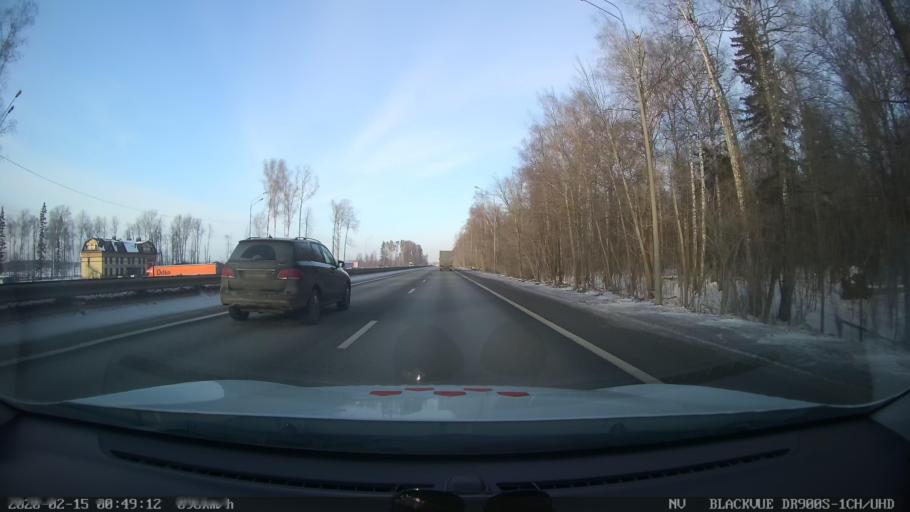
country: RU
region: Tatarstan
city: Osinovo
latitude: 55.8468
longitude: 48.8528
